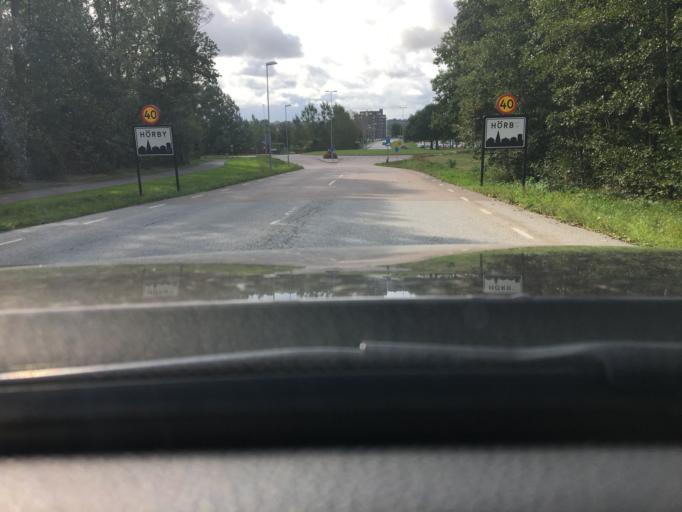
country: SE
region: Skane
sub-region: Horby Kommun
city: Hoerby
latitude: 55.8578
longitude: 13.6764
